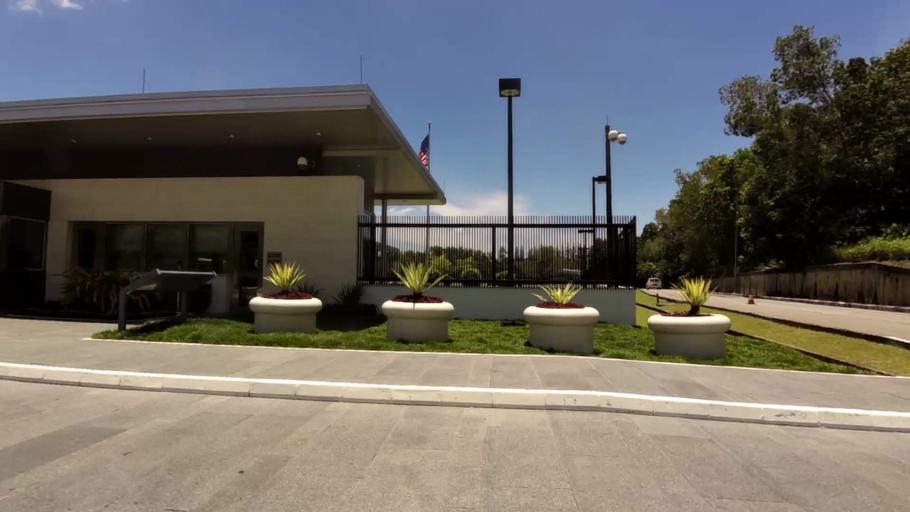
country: BN
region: Brunei and Muara
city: Bandar Seri Begawan
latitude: 4.9194
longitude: 114.9563
